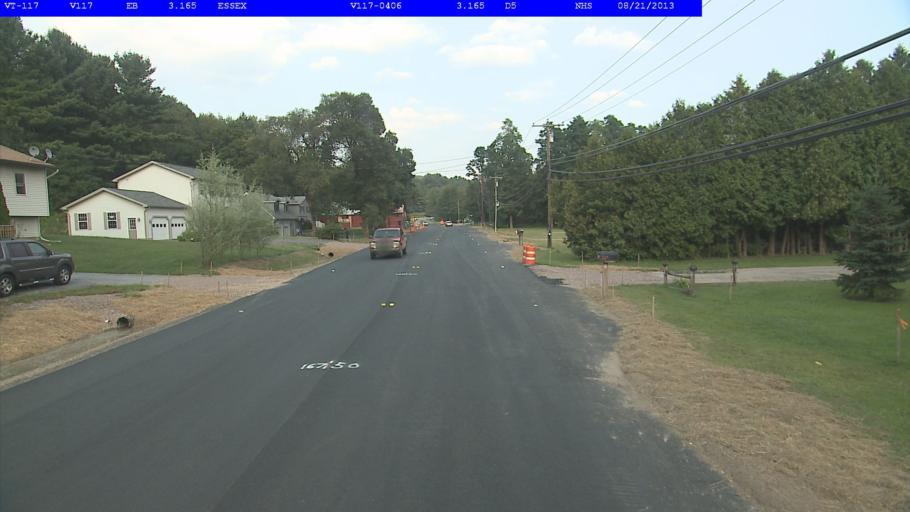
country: US
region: Vermont
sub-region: Chittenden County
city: Williston
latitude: 44.4789
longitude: -73.0516
